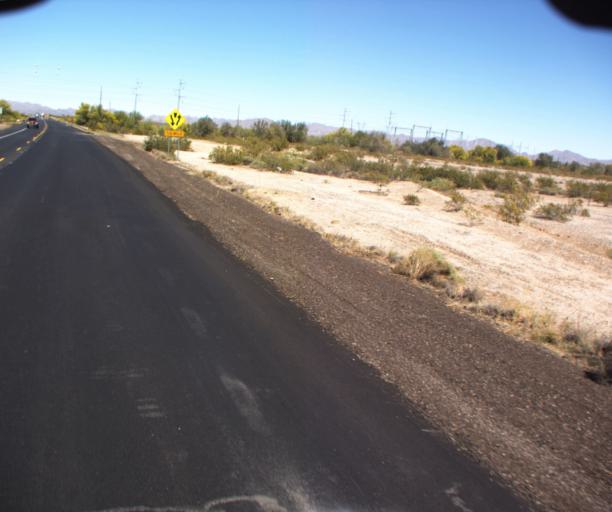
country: US
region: Arizona
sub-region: Maricopa County
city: Gila Bend
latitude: 32.9679
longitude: -112.6743
